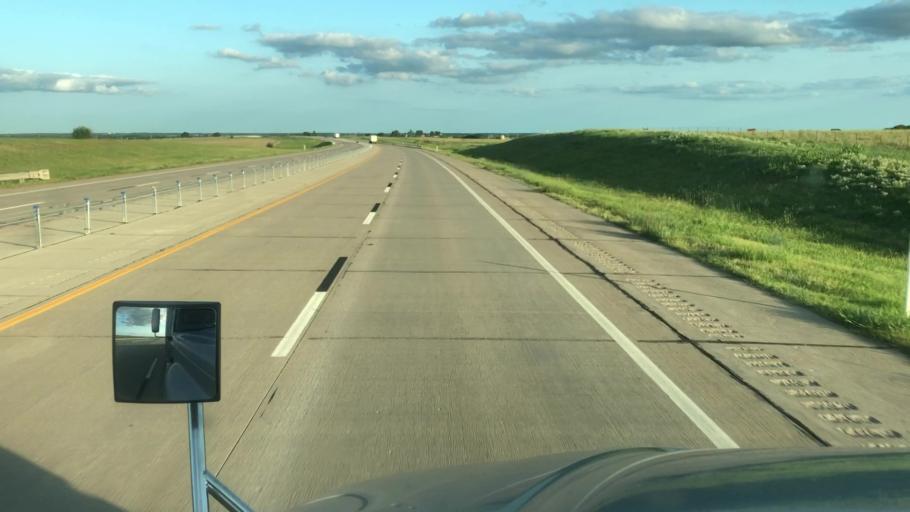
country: US
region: Oklahoma
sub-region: Pawnee County
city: Pawnee
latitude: 36.3444
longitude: -97.0264
